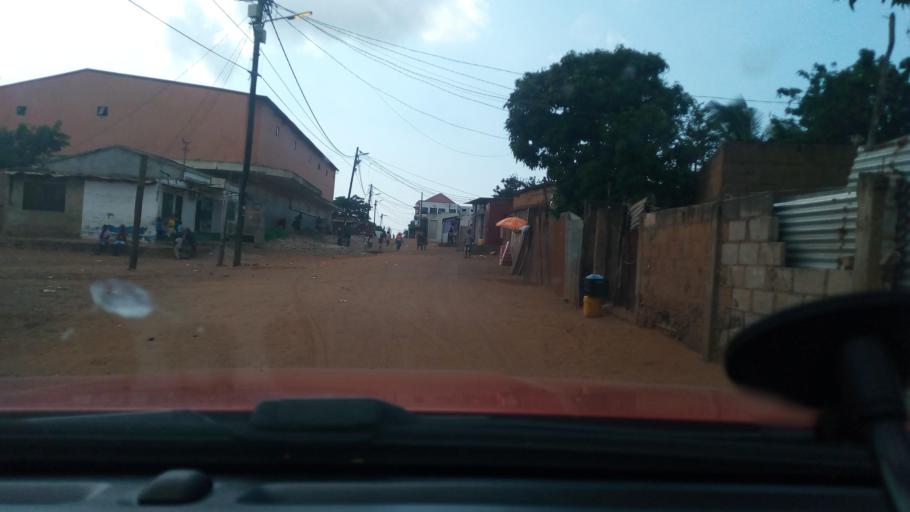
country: MZ
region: Maputo City
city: Maputo
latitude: -25.9218
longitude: 32.5933
